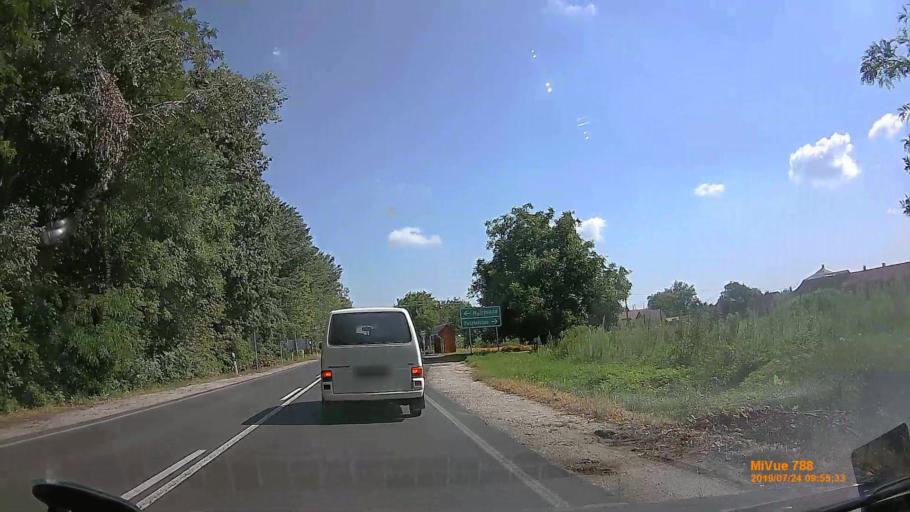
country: HU
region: Szabolcs-Szatmar-Bereg
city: Nyirmada
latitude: 48.0583
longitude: 22.2122
